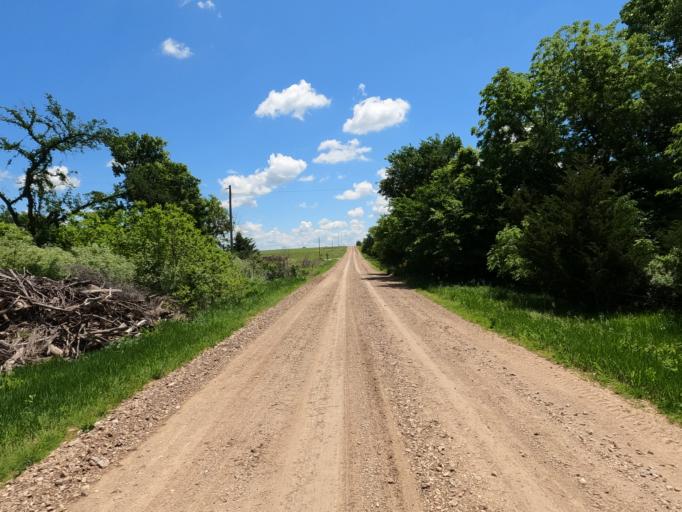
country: US
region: Kansas
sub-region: Marion County
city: Marion
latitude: 38.2164
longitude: -96.7849
